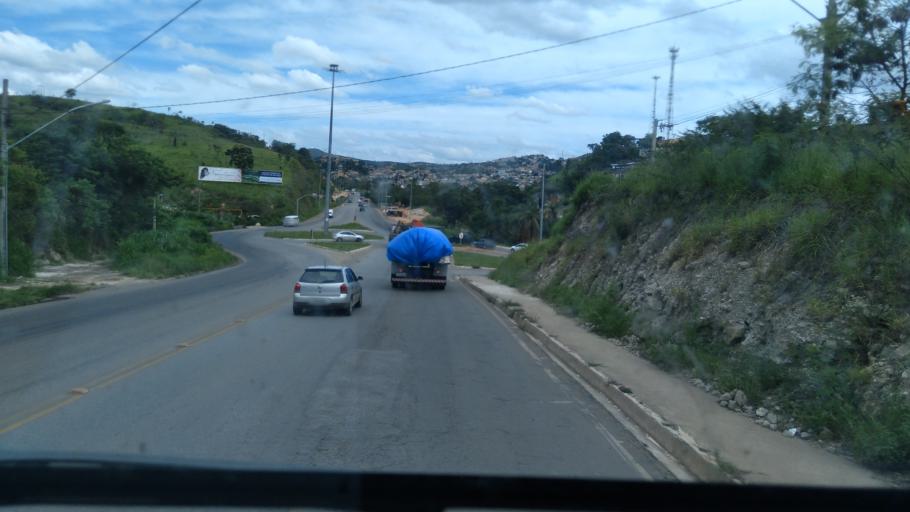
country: BR
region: Minas Gerais
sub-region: Belo Horizonte
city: Belo Horizonte
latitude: -19.8771
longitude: -43.8675
